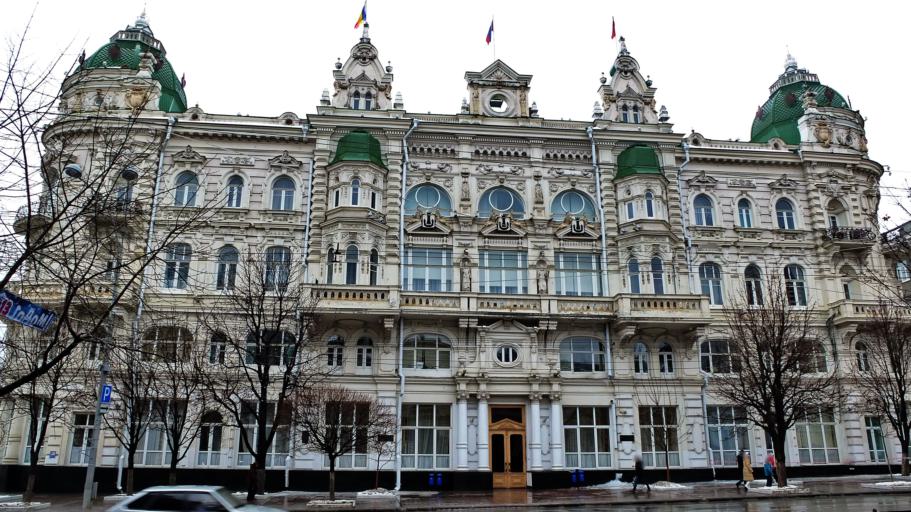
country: RU
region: Rostov
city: Rostov-na-Donu
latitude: 47.2210
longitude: 39.7126
